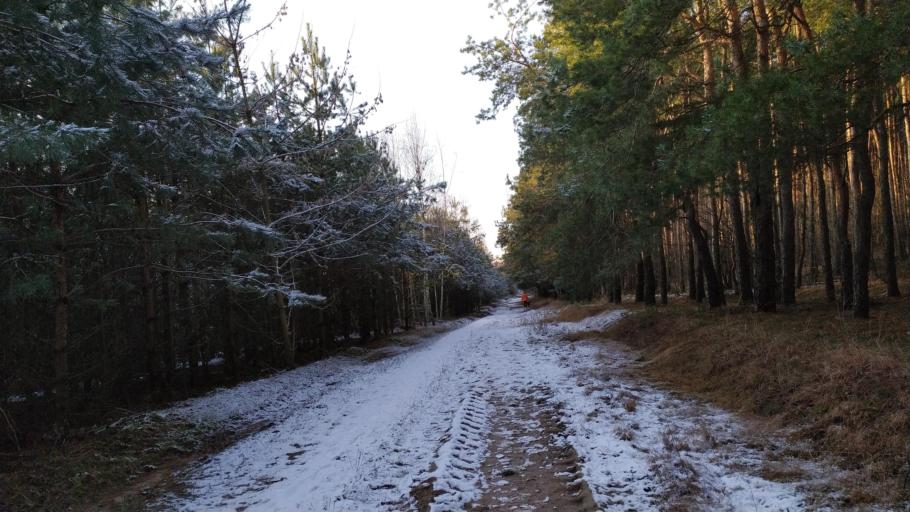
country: BY
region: Brest
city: Kamyanyets
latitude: 52.3830
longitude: 23.8328
